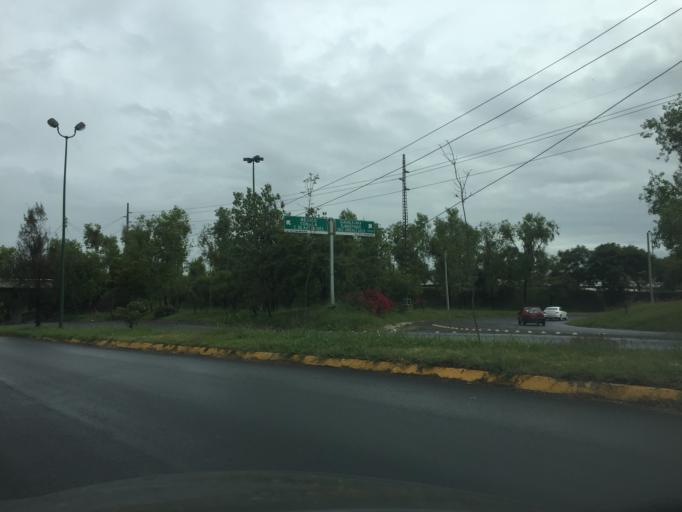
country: MX
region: Jalisco
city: Tlaquepaque
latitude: 20.6241
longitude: -103.3204
